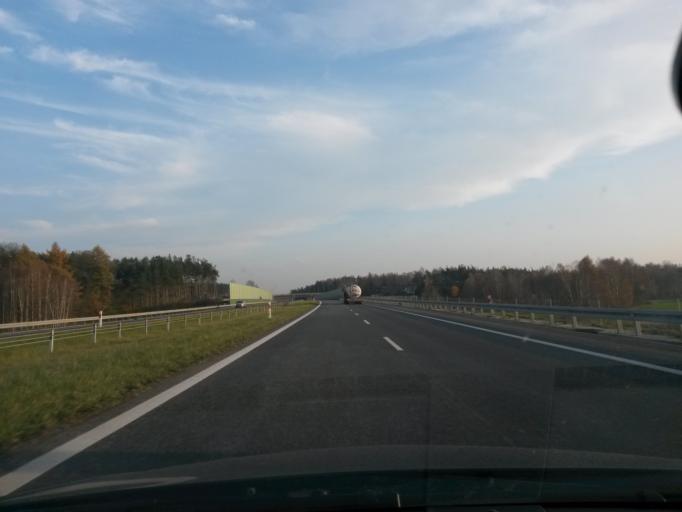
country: PL
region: Lodz Voivodeship
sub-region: Powiat wieruszowski
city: Wieruszow
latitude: 51.3127
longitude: 18.1730
